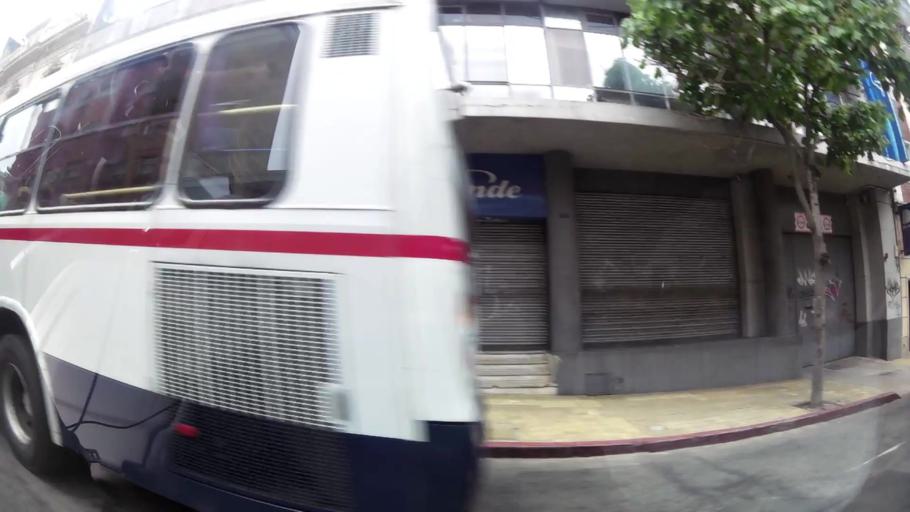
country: UY
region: Montevideo
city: Montevideo
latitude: -34.9023
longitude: -56.1943
